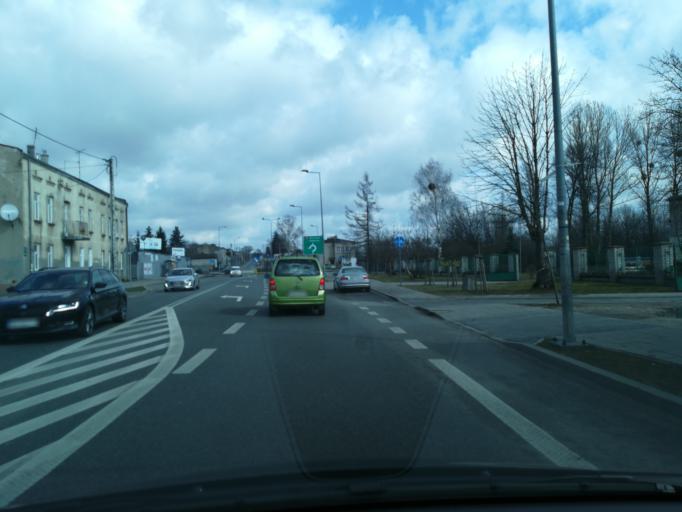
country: PL
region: Silesian Voivodeship
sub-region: Czestochowa
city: Czestochowa
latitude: 50.8228
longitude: 19.1332
